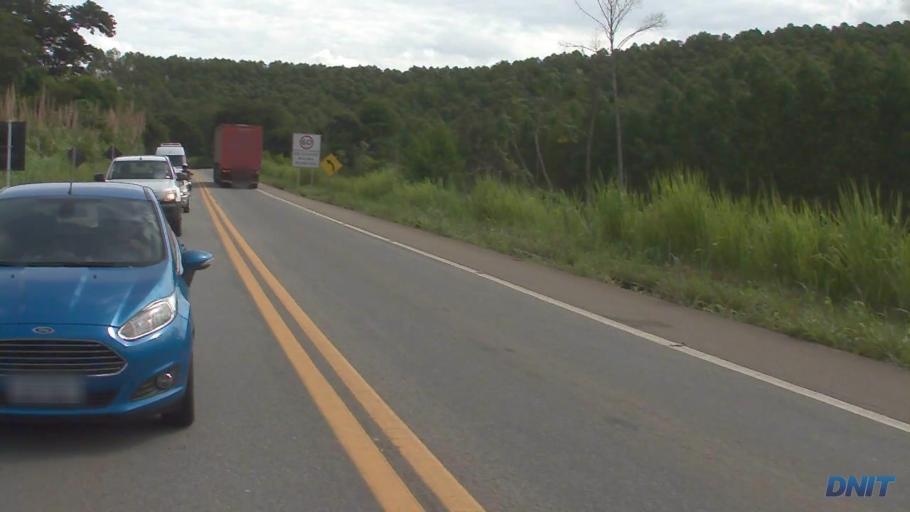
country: BR
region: Minas Gerais
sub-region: Ipaba
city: Ipaba
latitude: -19.3599
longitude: -42.4414
